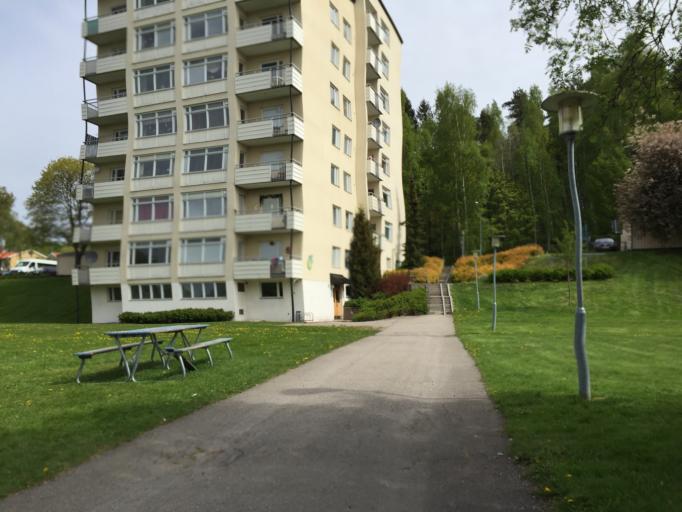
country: SE
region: Dalarna
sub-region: Ludvika Kommun
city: Ludvika
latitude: 60.1331
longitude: 15.1830
